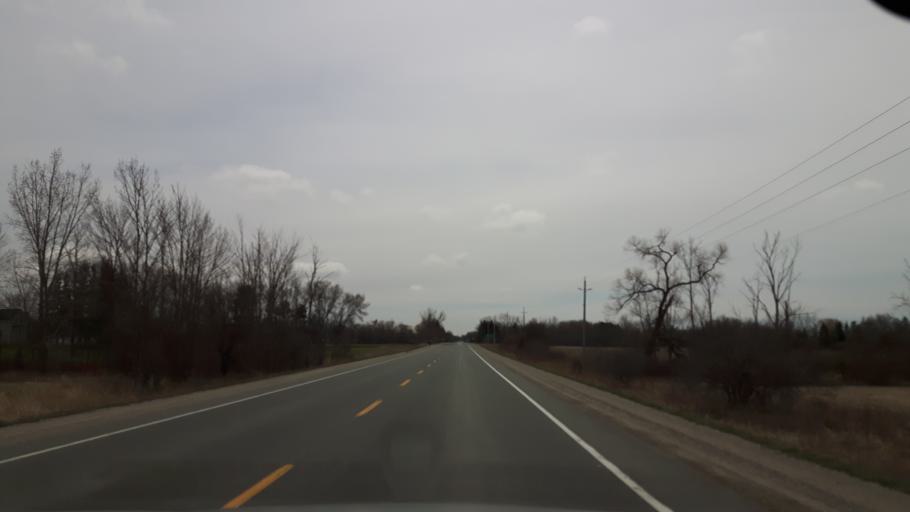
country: CA
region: Ontario
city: Goderich
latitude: 43.5952
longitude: -81.7057
